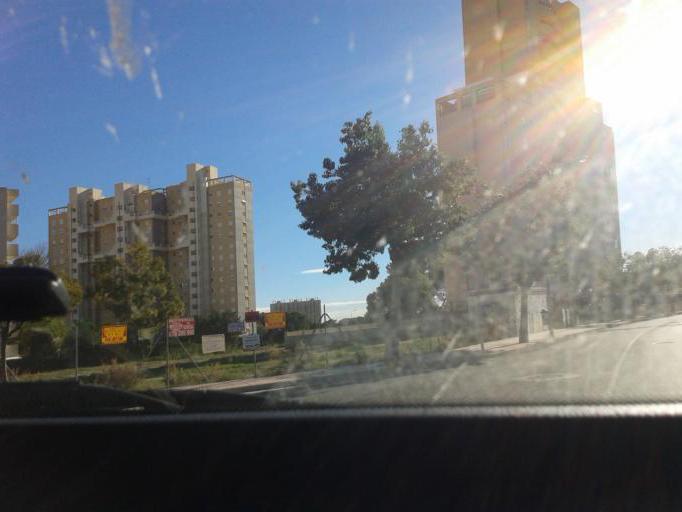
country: ES
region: Valencia
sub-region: Provincia de Alicante
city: San Juan de Alicante
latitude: 38.4045
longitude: -0.4096
